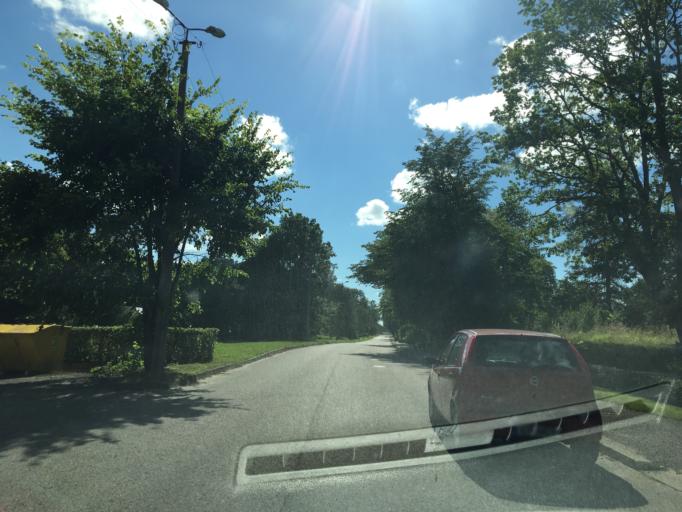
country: EE
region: Paernumaa
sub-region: Vaendra vald (alev)
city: Vandra
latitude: 58.6514
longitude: 25.0395
